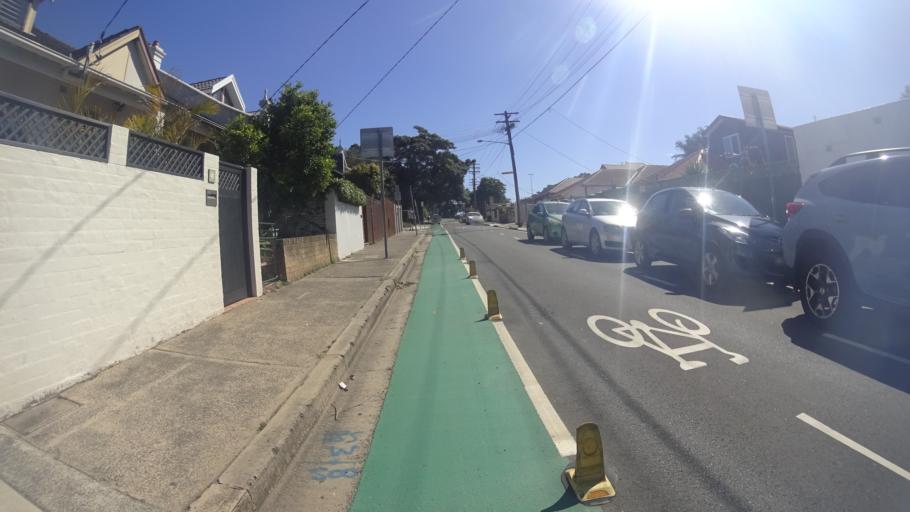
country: AU
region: New South Wales
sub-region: Waverley
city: Bondi
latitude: -33.8981
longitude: 151.2576
